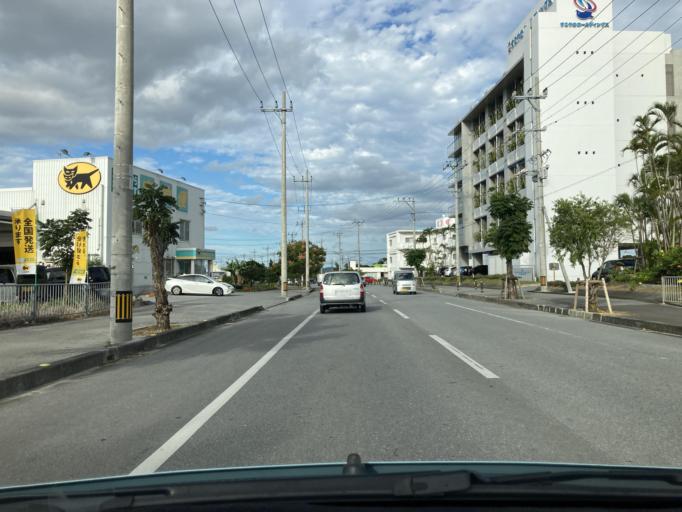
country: JP
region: Okinawa
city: Okinawa
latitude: 26.3691
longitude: 127.8259
